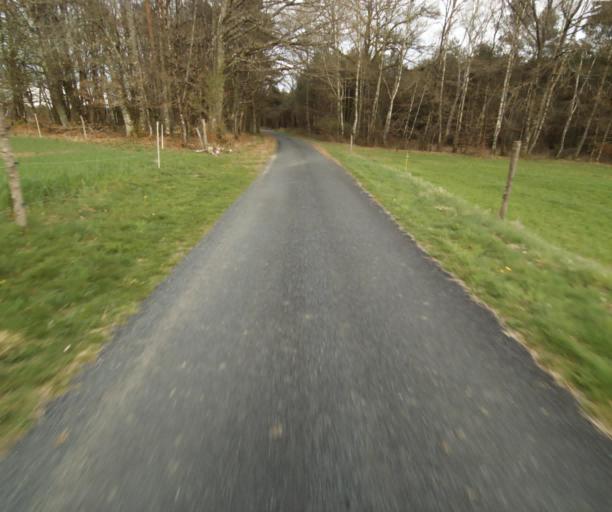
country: FR
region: Limousin
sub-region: Departement de la Correze
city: Saint-Privat
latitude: 45.1996
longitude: 1.9990
